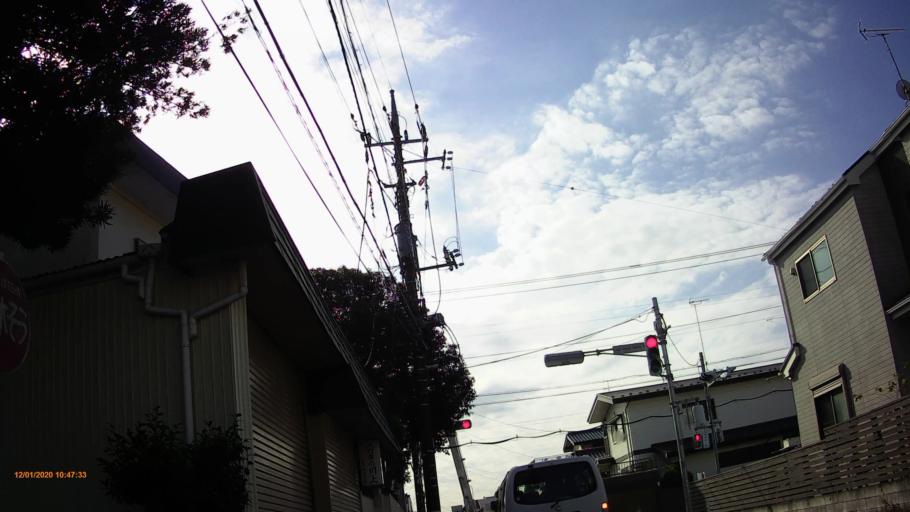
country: JP
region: Chiba
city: Yotsukaido
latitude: 35.6216
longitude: 140.1975
